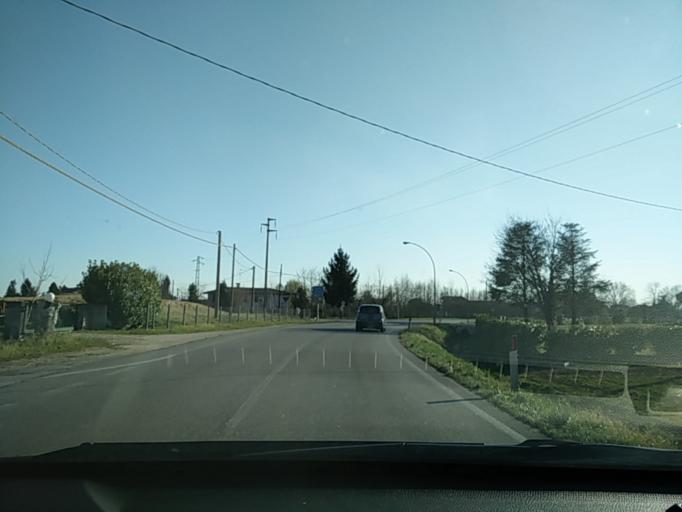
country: IT
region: Veneto
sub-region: Provincia di Treviso
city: Fontanelle
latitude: 45.8385
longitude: 12.4788
